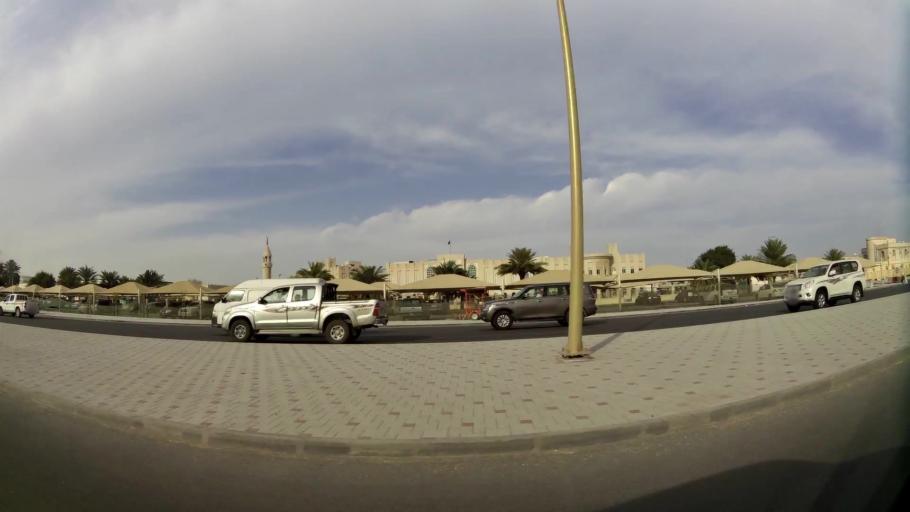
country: QA
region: Baladiyat ad Dawhah
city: Doha
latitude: 25.2507
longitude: 51.5379
